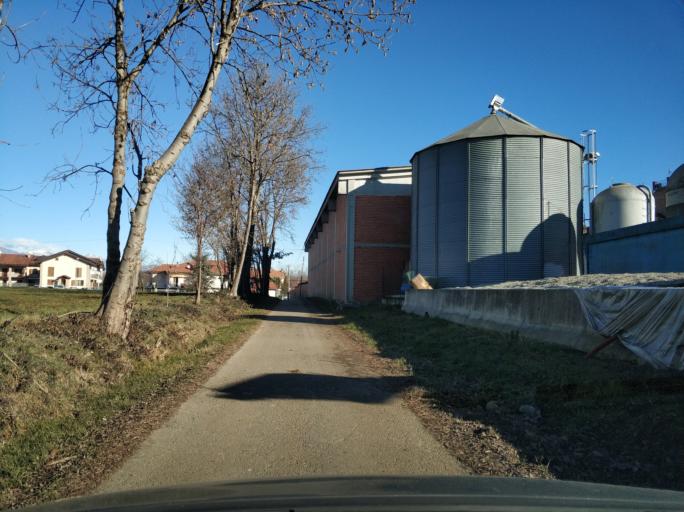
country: IT
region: Piedmont
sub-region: Provincia di Torino
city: San Francesco al Campo
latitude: 45.2377
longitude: 7.6490
